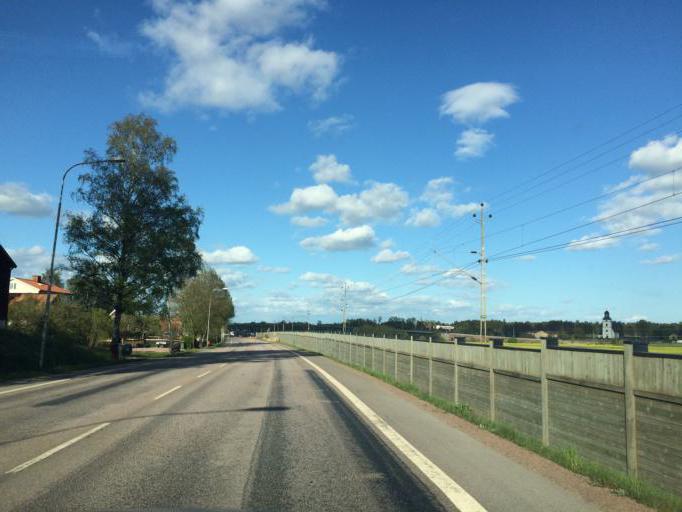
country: SE
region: Vaestmanland
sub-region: Hallstahammars Kommun
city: Kolback
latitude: 59.5572
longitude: 16.2162
